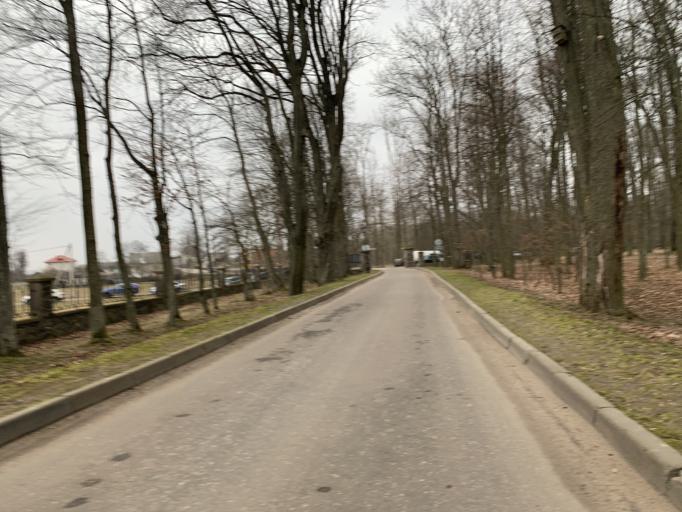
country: BY
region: Minsk
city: Nyasvizh
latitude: 53.2268
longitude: 26.6923
